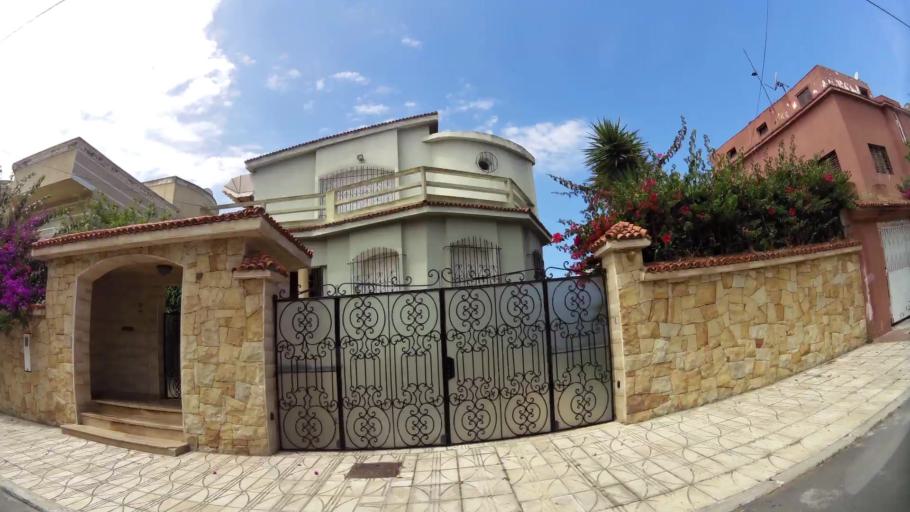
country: MA
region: Gharb-Chrarda-Beni Hssen
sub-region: Kenitra Province
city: Kenitra
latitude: 34.2549
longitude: -6.6020
